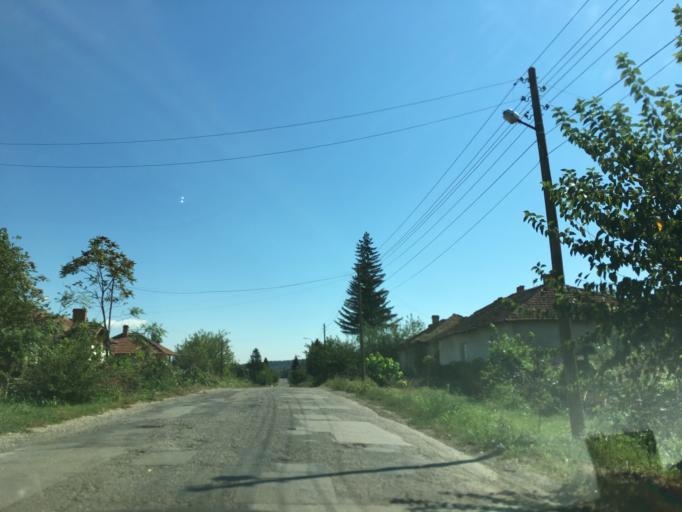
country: RO
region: Dolj
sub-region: Comuna Desa
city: Desa
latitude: 43.7699
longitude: 22.9995
